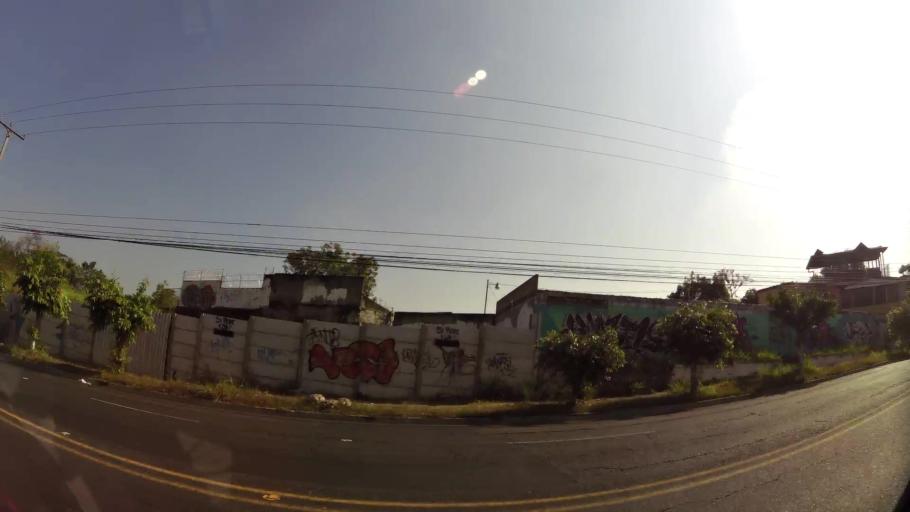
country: SV
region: La Libertad
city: Antiguo Cuscatlan
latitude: 13.6702
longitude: -89.2282
